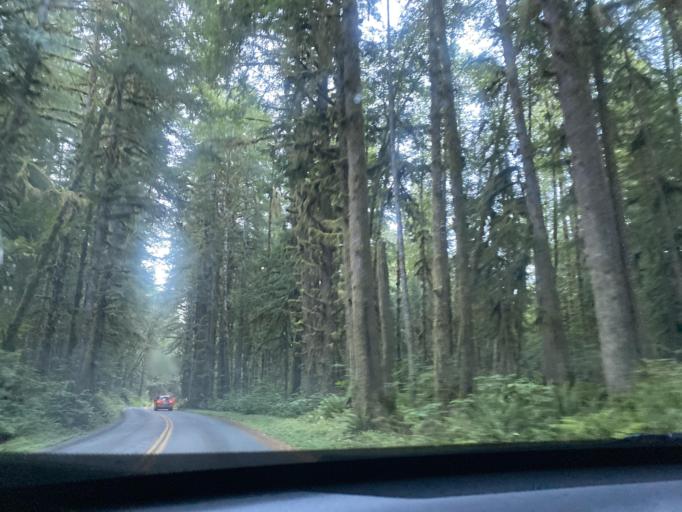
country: US
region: Washington
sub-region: Clallam County
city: Forks
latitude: 47.8145
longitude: -124.1074
